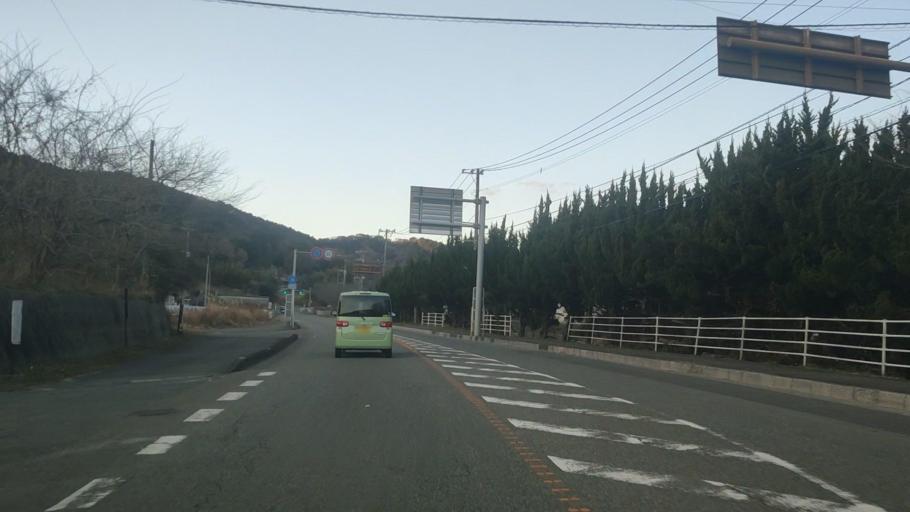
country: JP
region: Fukuoka
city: Dazaifu
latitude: 33.5377
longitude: 130.5402
